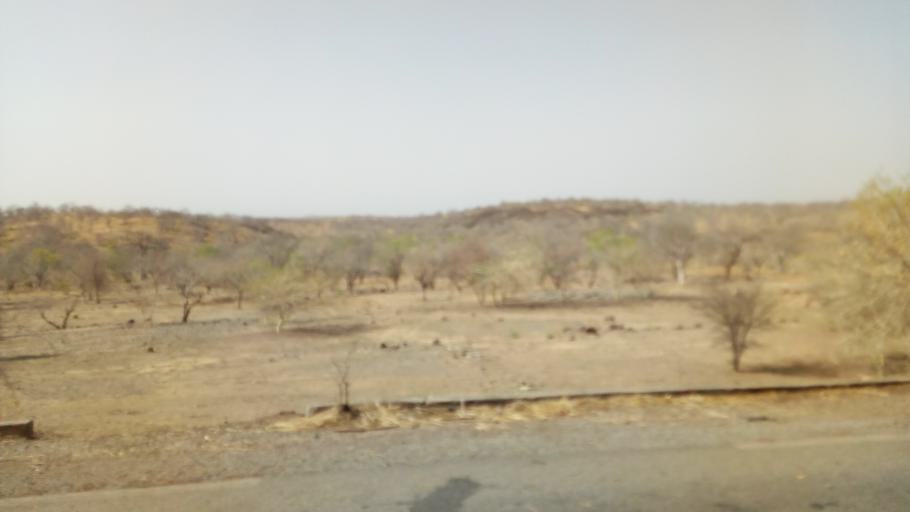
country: ML
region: Kayes
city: Yelimane
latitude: 14.6452
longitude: -10.6602
